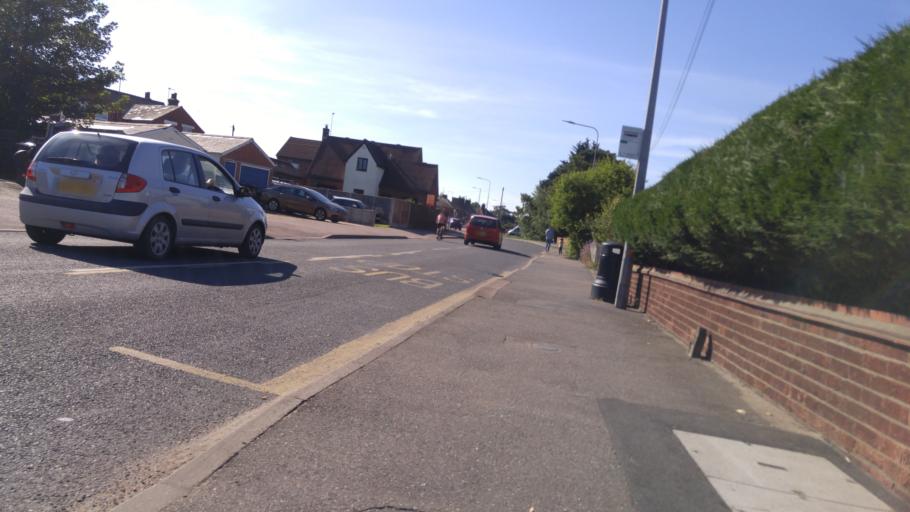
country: GB
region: England
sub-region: Essex
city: Rowhedge
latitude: 51.8671
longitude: 0.9296
